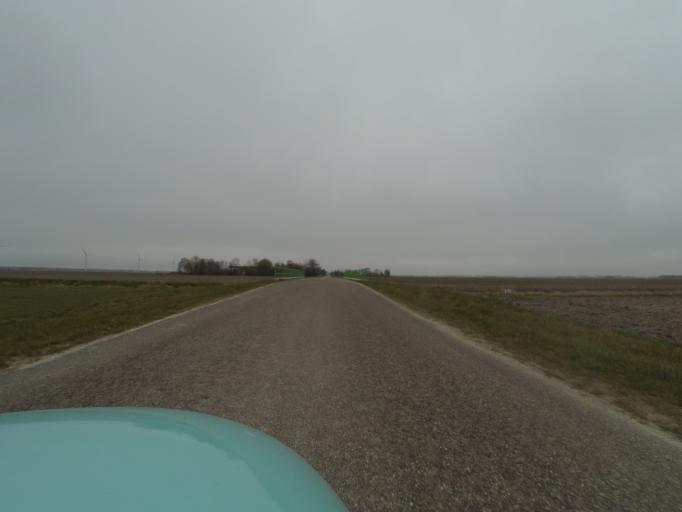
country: NL
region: Flevoland
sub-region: Gemeente Dronten
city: Dronten
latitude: 52.4865
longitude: 5.7687
